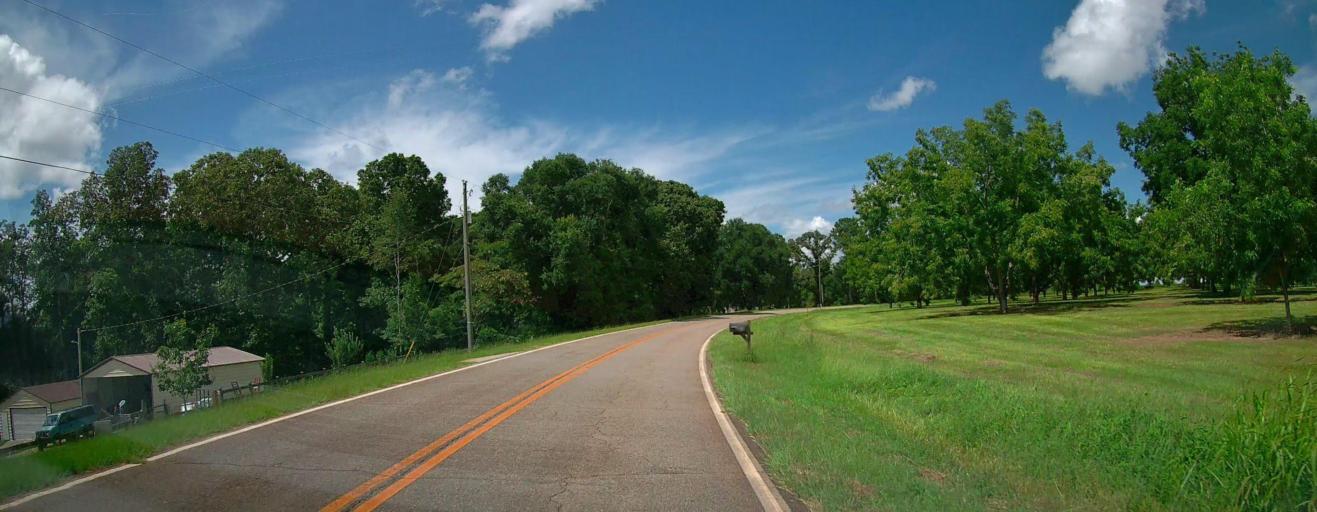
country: US
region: Georgia
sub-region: Peach County
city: Fort Valley
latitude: 32.5232
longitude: -83.8015
